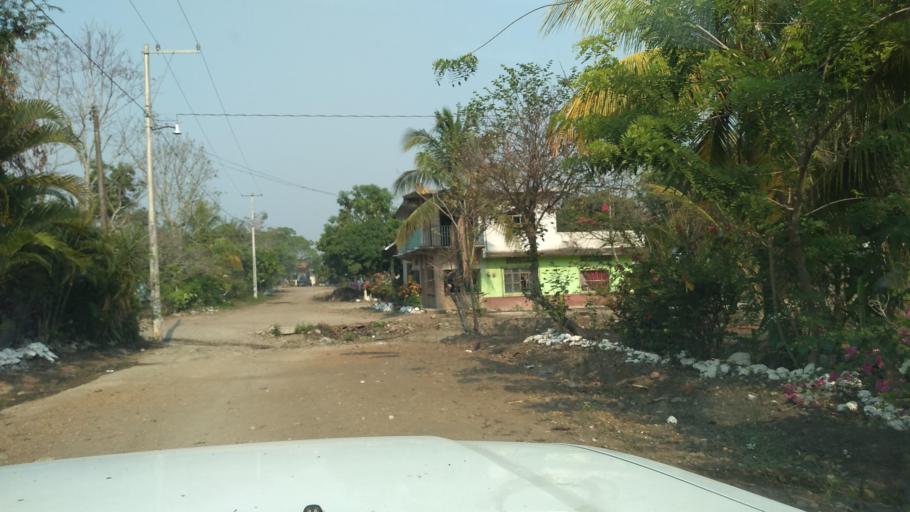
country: MX
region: Oaxaca
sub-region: Cosolapa
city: Cosolapa
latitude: 18.6239
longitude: -96.6018
